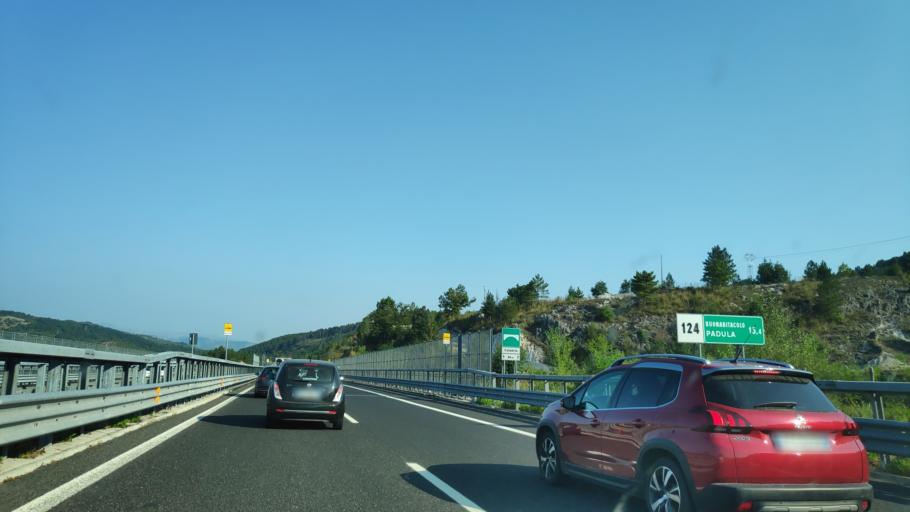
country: IT
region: Campania
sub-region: Provincia di Salerno
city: Casalbuono
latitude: 40.1760
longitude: 15.7172
